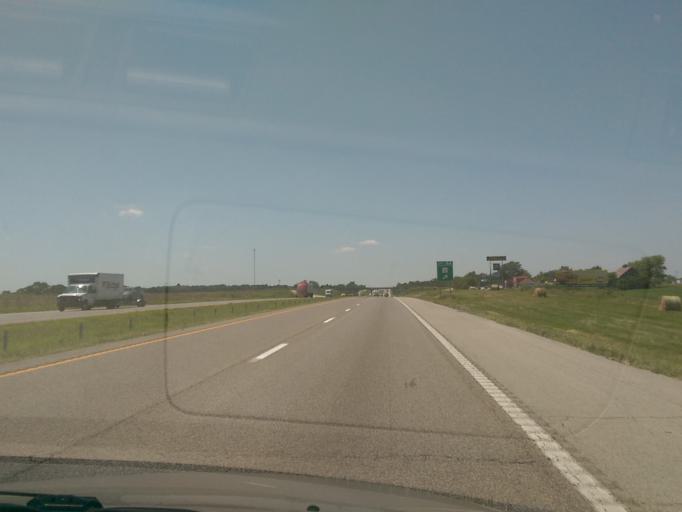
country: US
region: Missouri
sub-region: Saline County
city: Marshall
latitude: 38.9528
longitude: -93.0826
